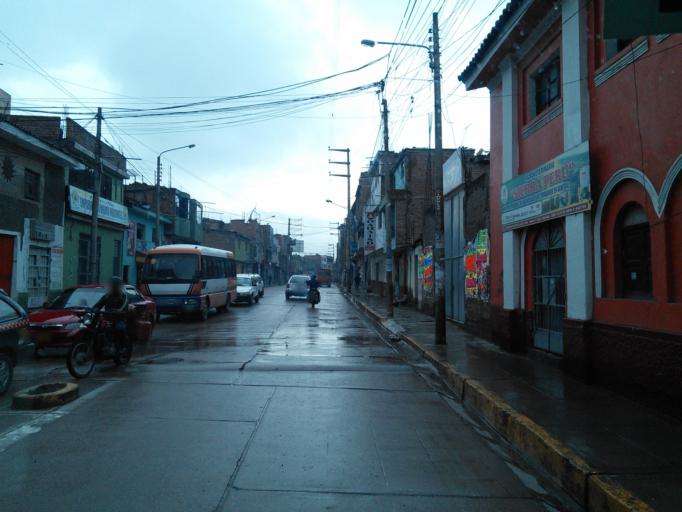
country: PE
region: Ayacucho
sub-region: Provincia de Huamanga
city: Ayacucho
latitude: -13.1642
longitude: -74.2206
